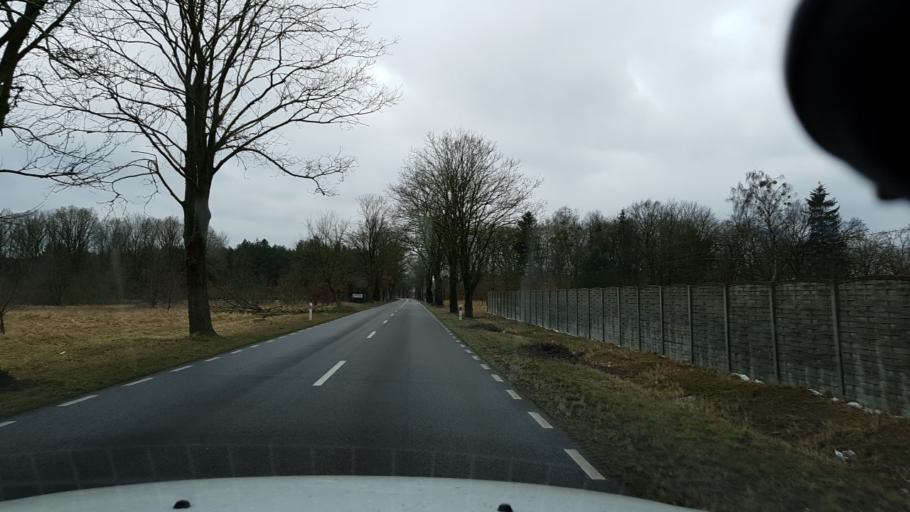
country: PL
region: West Pomeranian Voivodeship
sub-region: Powiat goleniowski
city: Goleniow
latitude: 53.6098
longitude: 14.7406
